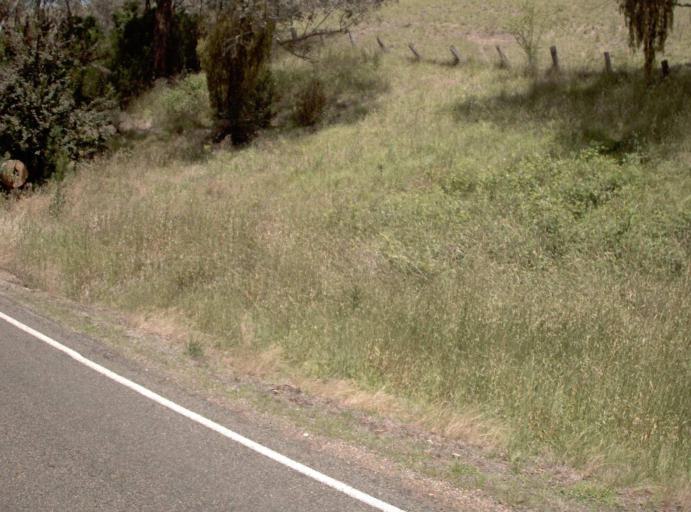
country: AU
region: Victoria
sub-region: East Gippsland
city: Bairnsdale
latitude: -37.4106
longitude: 147.8352
